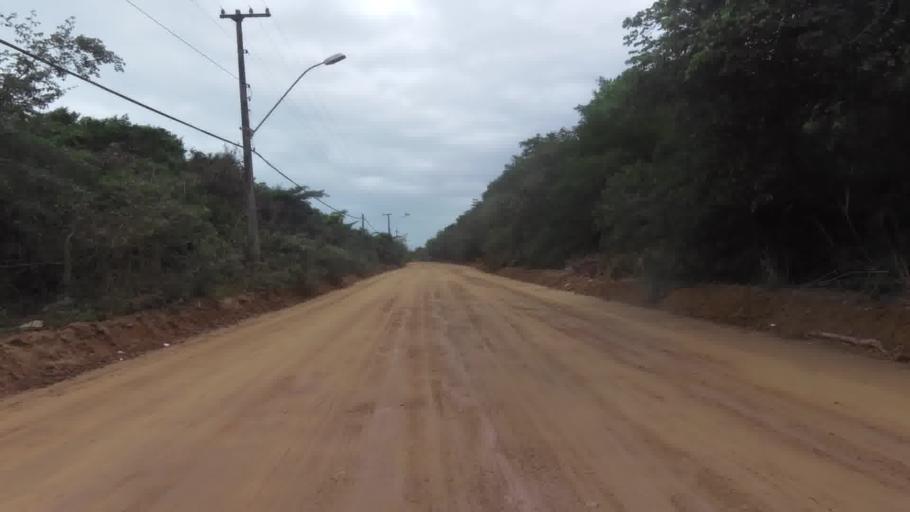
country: BR
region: Espirito Santo
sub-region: Marataizes
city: Marataizes
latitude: -21.0590
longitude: -40.8363
